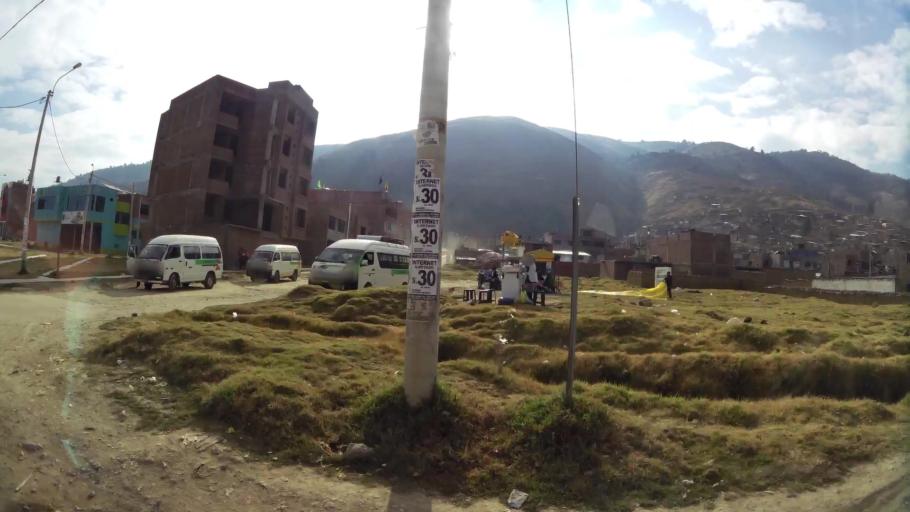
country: PE
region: Junin
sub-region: Provincia de Huancayo
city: Huancayo
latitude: -12.0514
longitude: -75.1881
